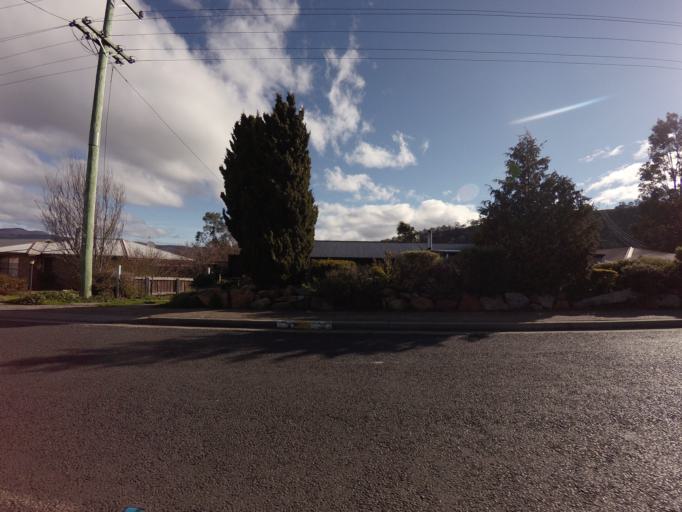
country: AU
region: Tasmania
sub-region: Derwent Valley
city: New Norfolk
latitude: -42.7594
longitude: 147.0471
